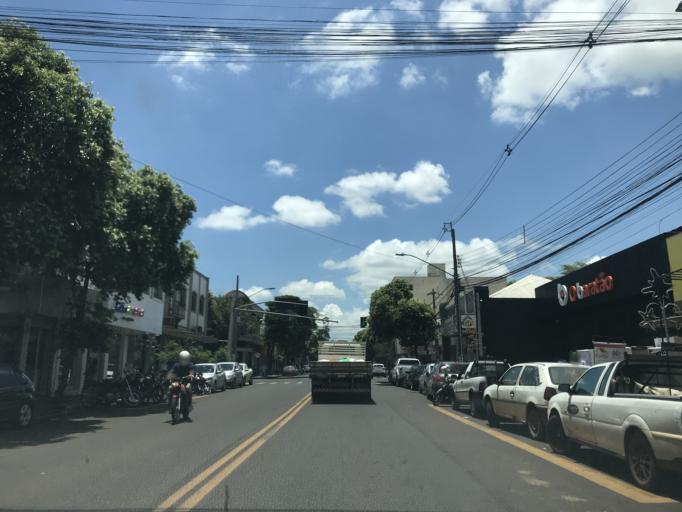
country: BR
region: Parana
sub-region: Marialva
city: Marialva
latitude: -23.4869
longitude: -51.7961
